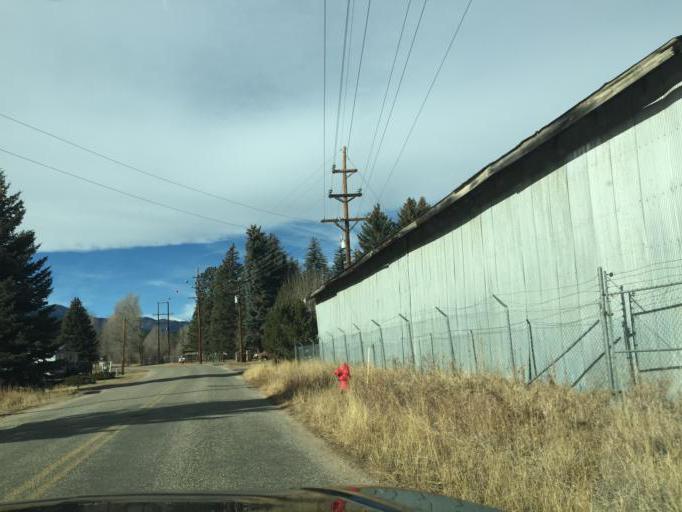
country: US
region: Colorado
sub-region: Jefferson County
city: Evergreen
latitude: 39.4059
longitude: -105.4793
